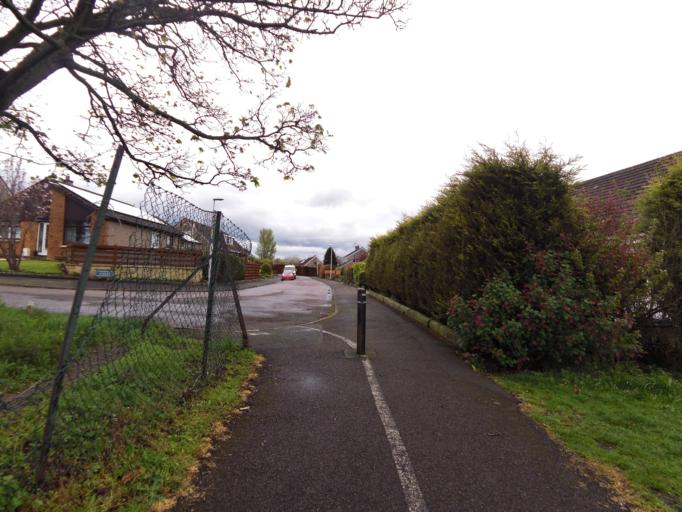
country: GB
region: Scotland
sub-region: Edinburgh
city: Queensferry
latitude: 55.9865
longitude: -3.4006
